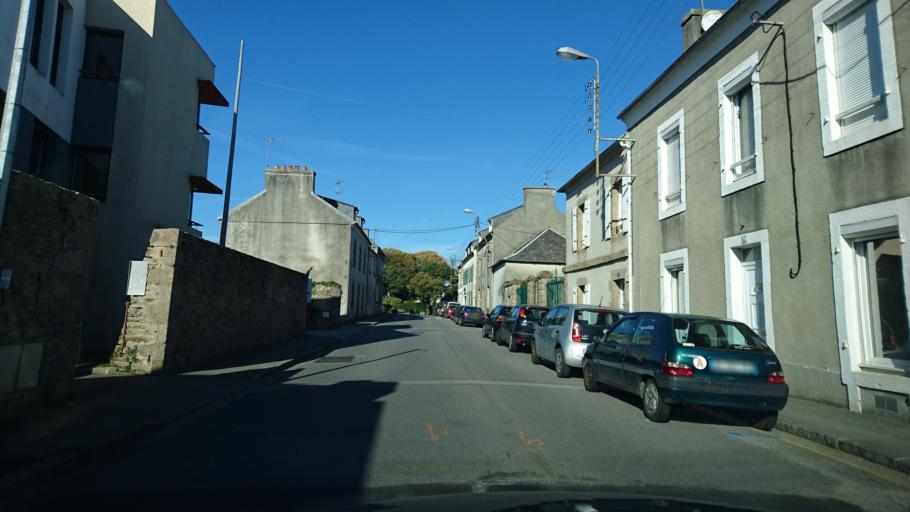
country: FR
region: Brittany
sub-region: Departement du Finistere
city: Saint-Renan
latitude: 48.4303
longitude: -4.6197
